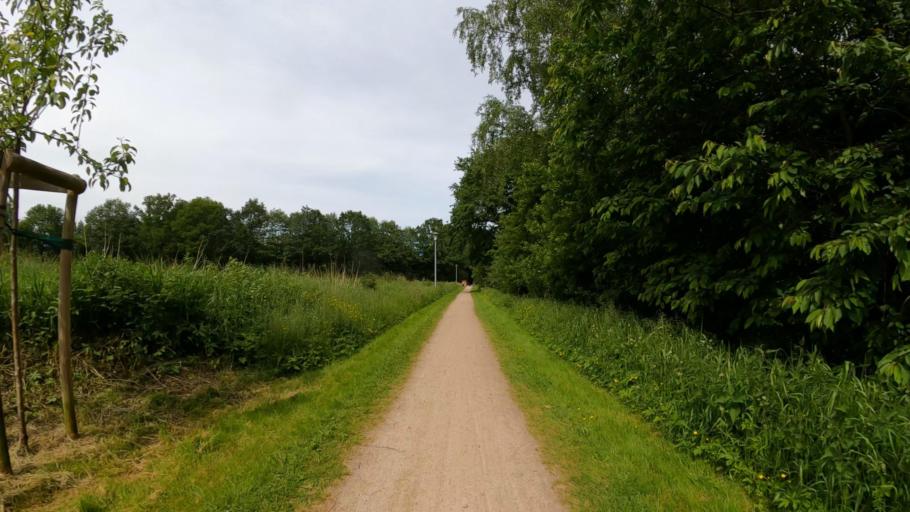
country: DE
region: Schleswig-Holstein
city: Nahe
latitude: 53.7892
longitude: 10.0875
